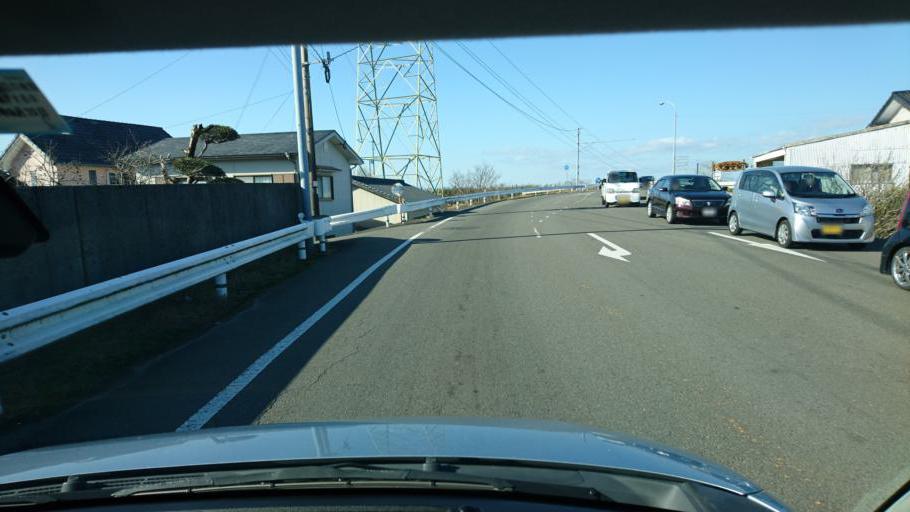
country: JP
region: Miyazaki
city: Miyazaki-shi
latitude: 31.8334
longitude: 131.4378
